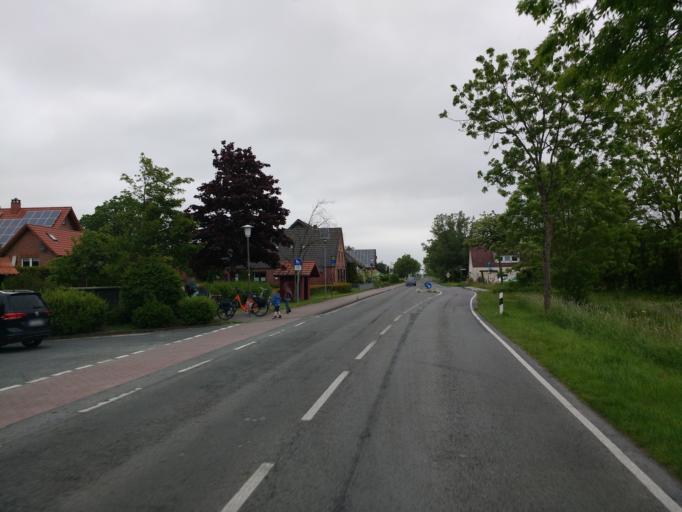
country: DE
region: Lower Saxony
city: Jever
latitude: 53.6349
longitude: 7.9231
